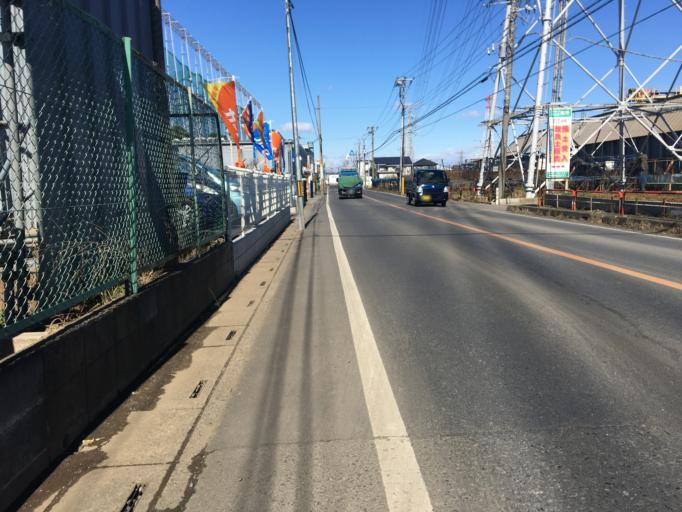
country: JP
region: Saitama
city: Asaka
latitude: 35.7889
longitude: 139.5534
